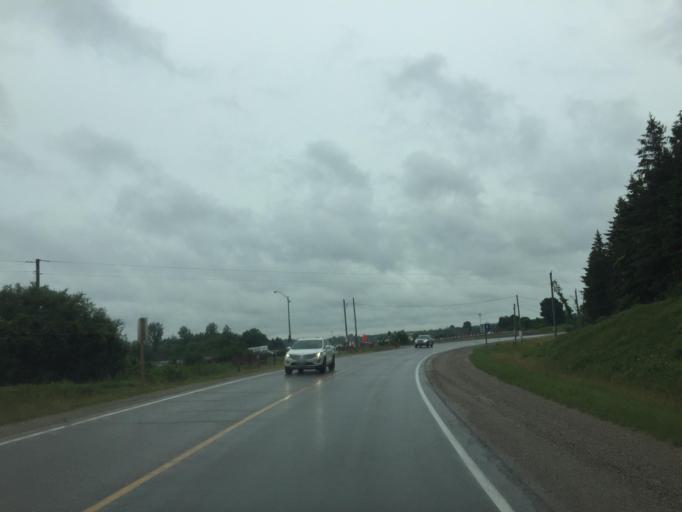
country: CA
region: Ontario
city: Cambridge
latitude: 43.4191
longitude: -80.2811
